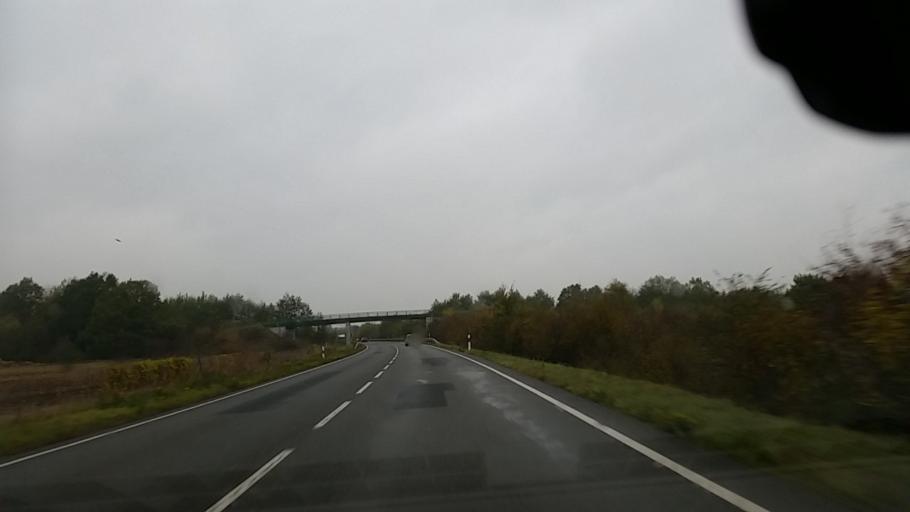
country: DE
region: Lower Saxony
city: Handorf
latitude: 53.3223
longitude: 10.3406
